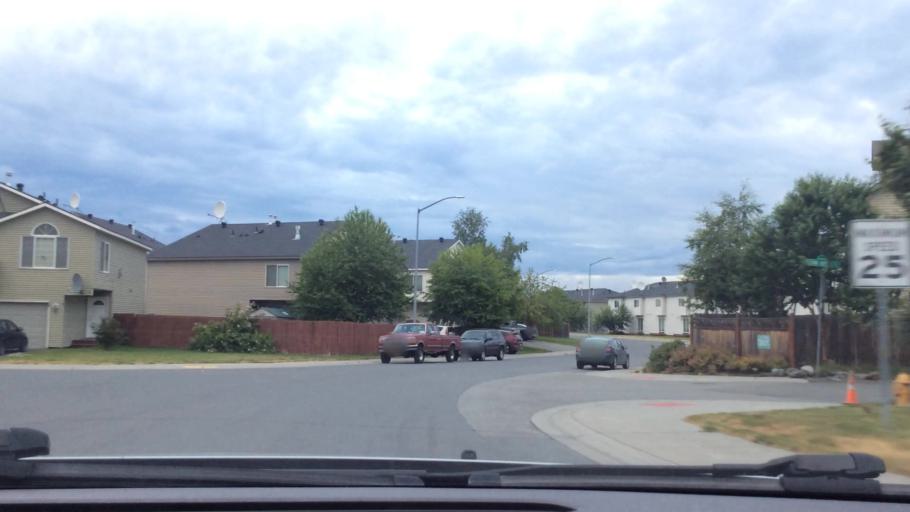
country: US
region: Alaska
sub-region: Anchorage Municipality
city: Elmendorf Air Force Base
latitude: 61.2219
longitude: -149.7565
